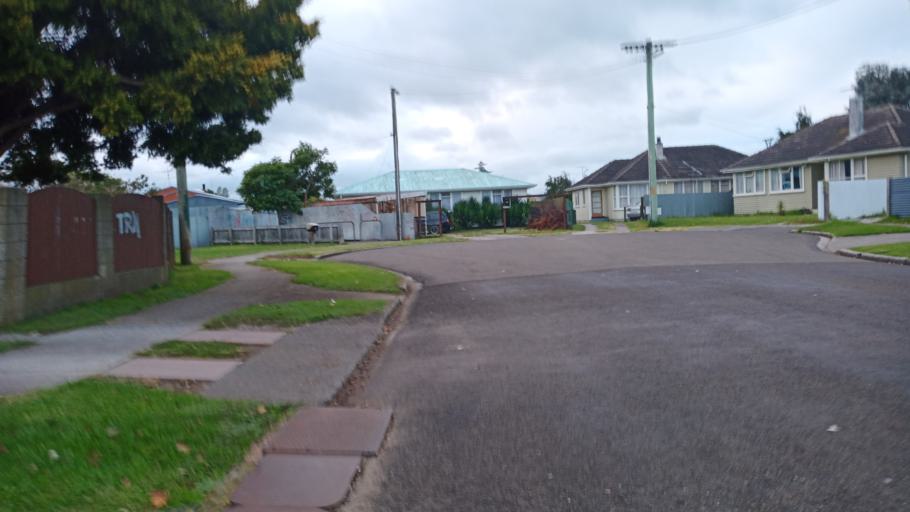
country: NZ
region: Gisborne
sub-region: Gisborne District
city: Gisborne
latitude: -38.6590
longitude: 177.9931
